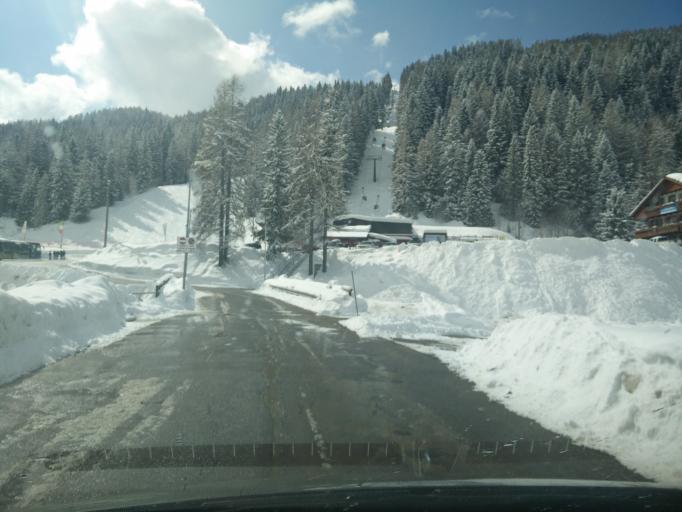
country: IT
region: Veneto
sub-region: Provincia di Belluno
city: Fusine
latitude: 46.3922
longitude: 12.1006
